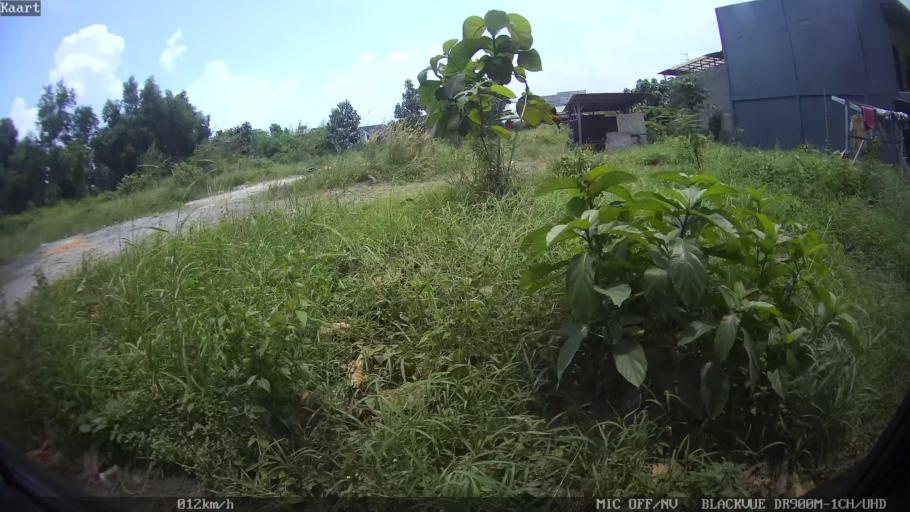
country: ID
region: Lampung
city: Kedaton
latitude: -5.3520
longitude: 105.2400
